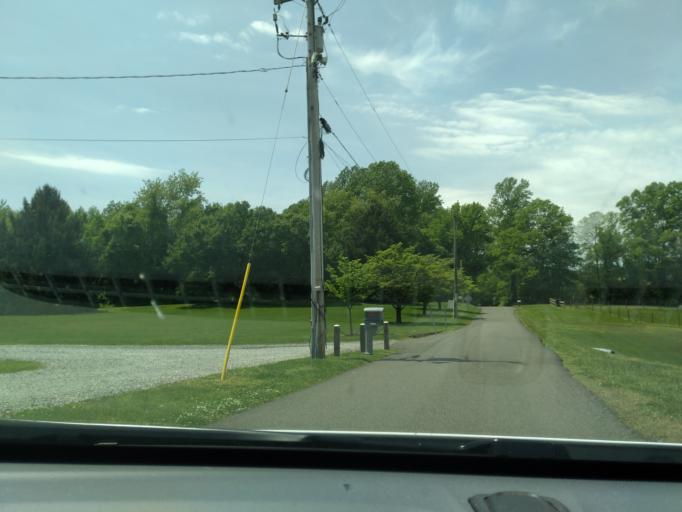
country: US
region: Maryland
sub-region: Prince George's County
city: Marlboro Meadows
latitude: 38.8544
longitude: -76.7156
